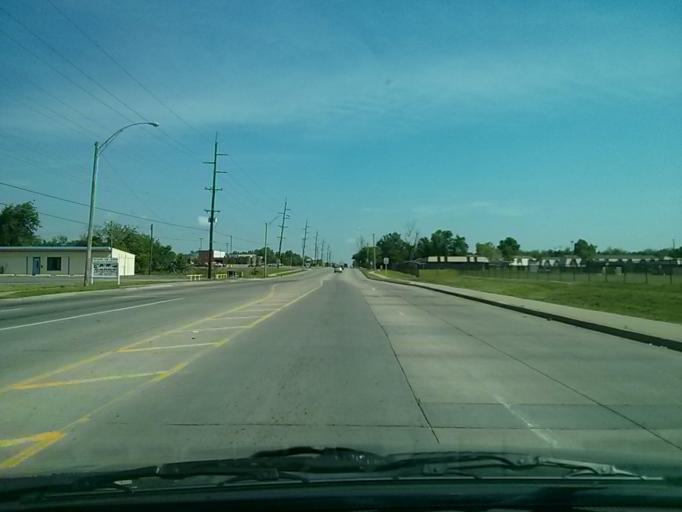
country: US
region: Oklahoma
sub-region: Tulsa County
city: Turley
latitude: 36.2063
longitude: -95.9755
